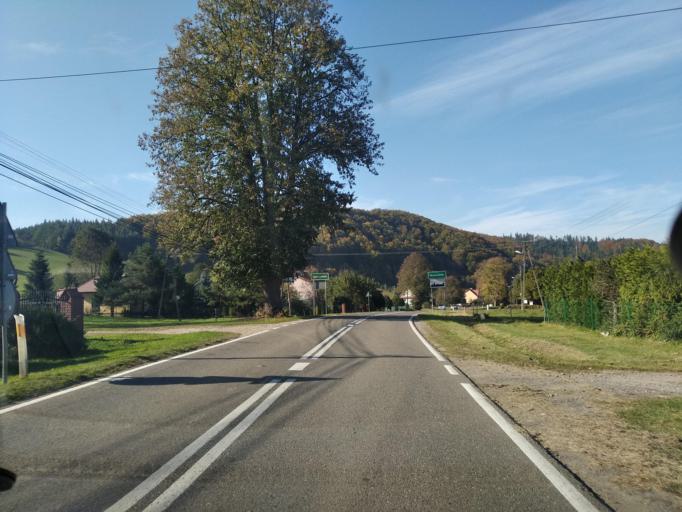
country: PL
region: Subcarpathian Voivodeship
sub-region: Powiat leski
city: Baligrod
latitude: 49.3920
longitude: 22.2835
